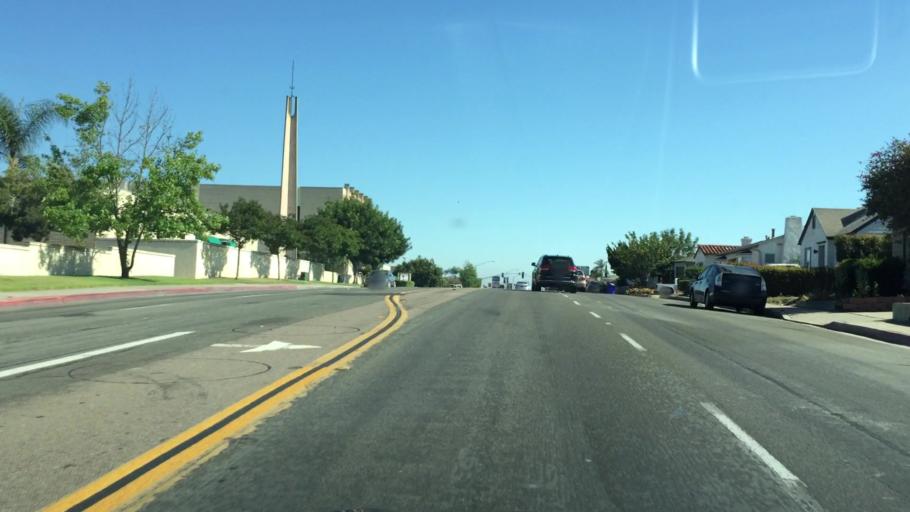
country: US
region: California
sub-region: San Diego County
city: Lemon Grove
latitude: 32.7650
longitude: -117.0669
